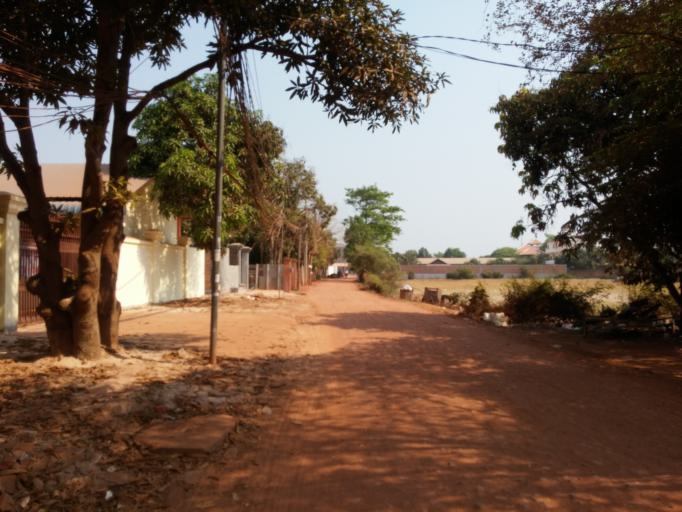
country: KH
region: Siem Reap
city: Siem Reap
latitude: 13.3723
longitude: 103.8480
